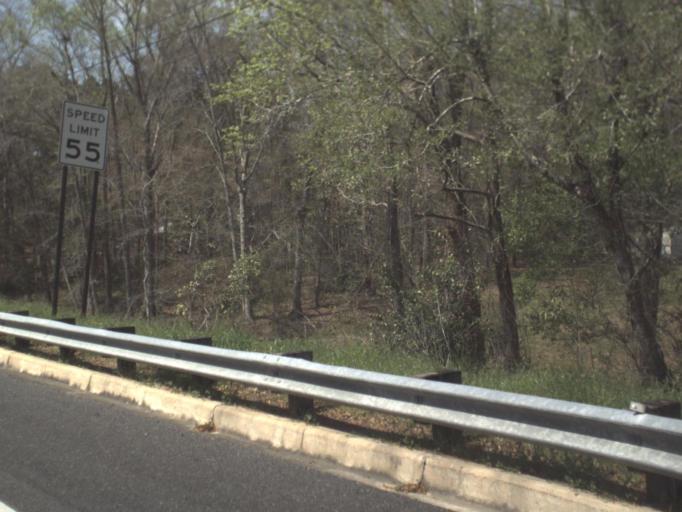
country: US
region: Florida
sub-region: Gadsden County
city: Quincy
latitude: 30.5545
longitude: -84.5242
